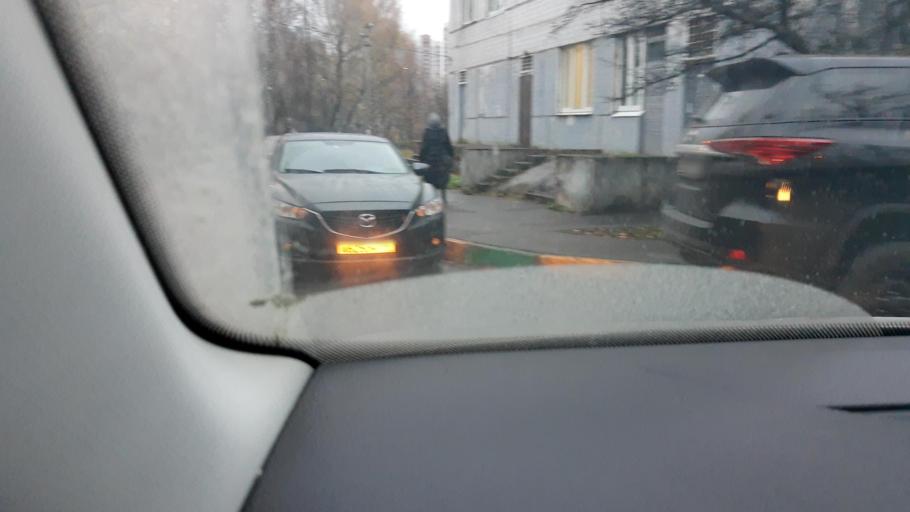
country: RU
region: Moskovskaya
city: Shcherbinka
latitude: 55.5327
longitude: 37.5892
